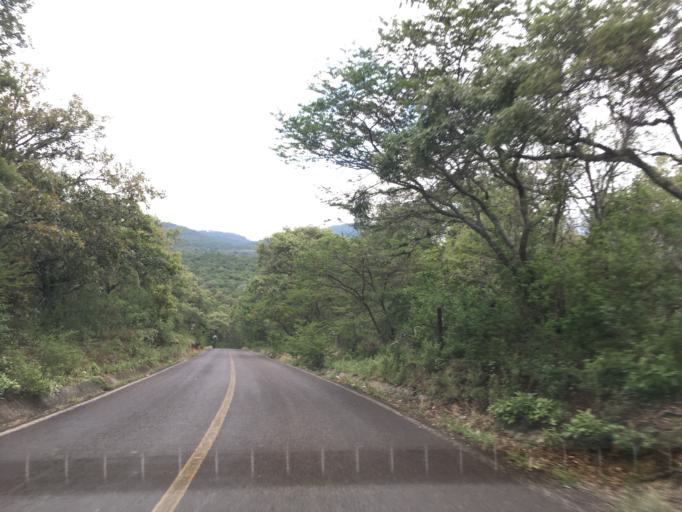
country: MX
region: Michoacan
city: Acuitzio del Canje
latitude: 19.5506
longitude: -101.2611
